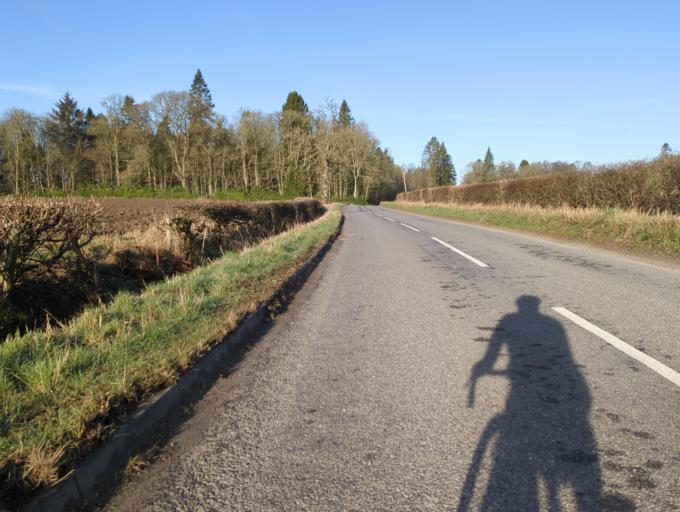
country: GB
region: Scotland
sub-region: Perth and Kinross
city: Methven
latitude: 56.4539
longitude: -3.5397
